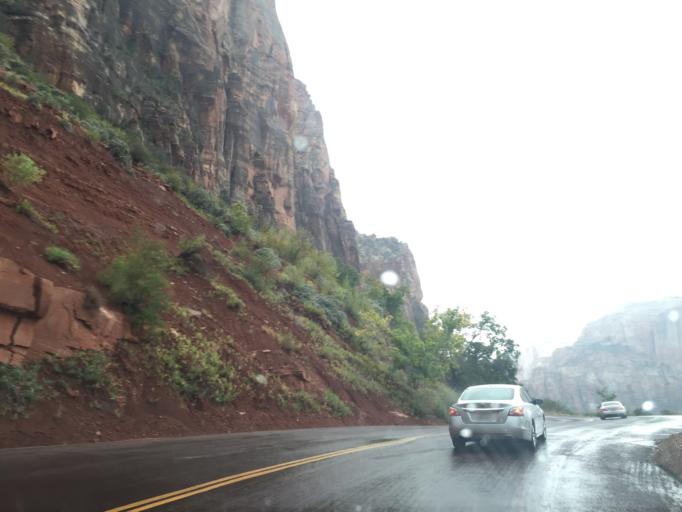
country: US
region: Utah
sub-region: Washington County
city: Hildale
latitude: 37.2119
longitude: -112.9563
